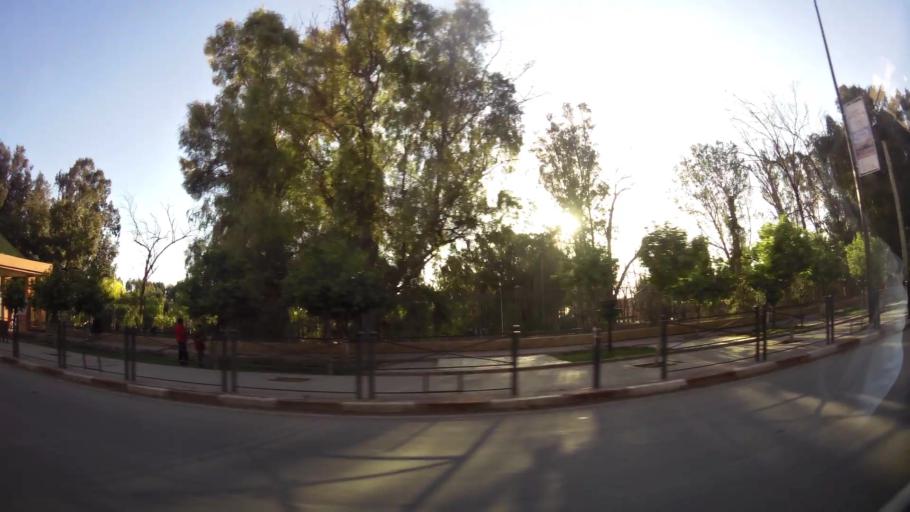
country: MA
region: Marrakech-Tensift-Al Haouz
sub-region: Kelaa-Des-Sraghna
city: Sidi Abdallah
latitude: 32.2329
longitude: -7.9578
